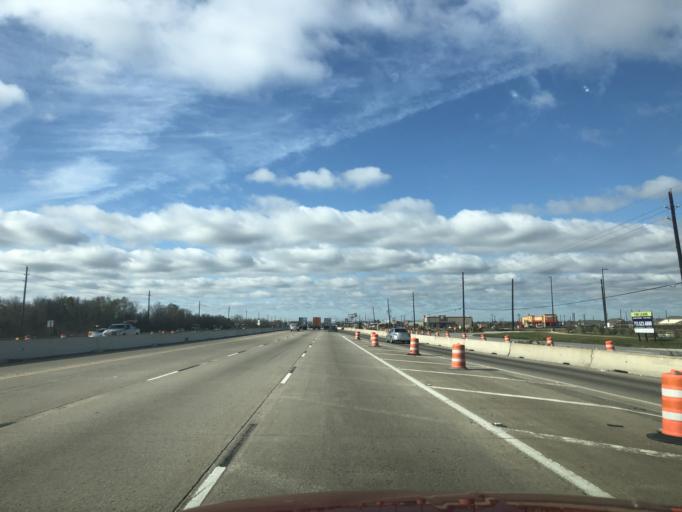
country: US
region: Texas
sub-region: Chambers County
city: Old River-Winfree
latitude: 29.8260
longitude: -94.8491
